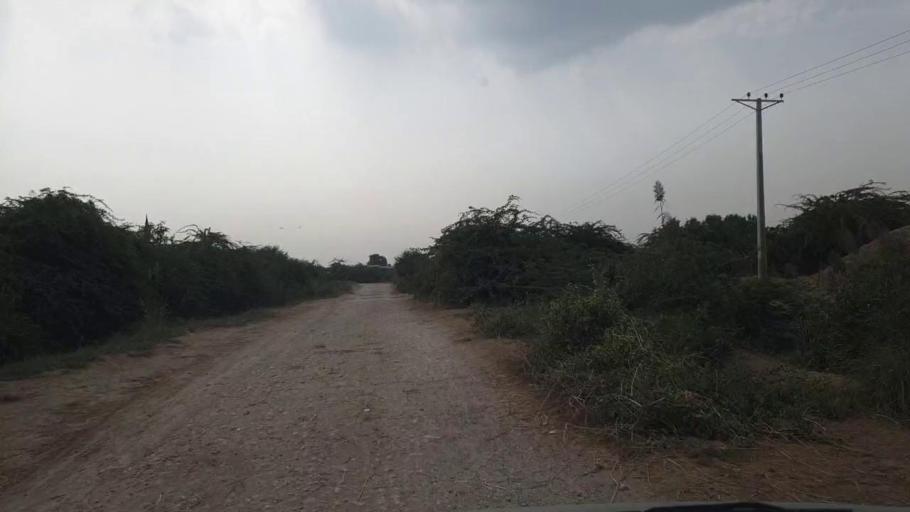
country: PK
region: Sindh
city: Talhar
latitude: 24.9054
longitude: 68.7708
